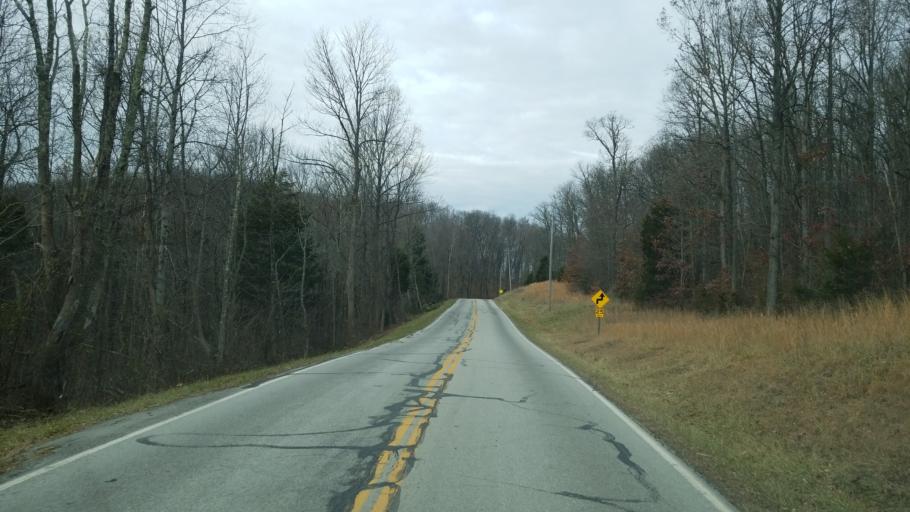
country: US
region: Ohio
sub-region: Highland County
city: Greenfield
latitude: 39.1900
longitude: -83.3621
